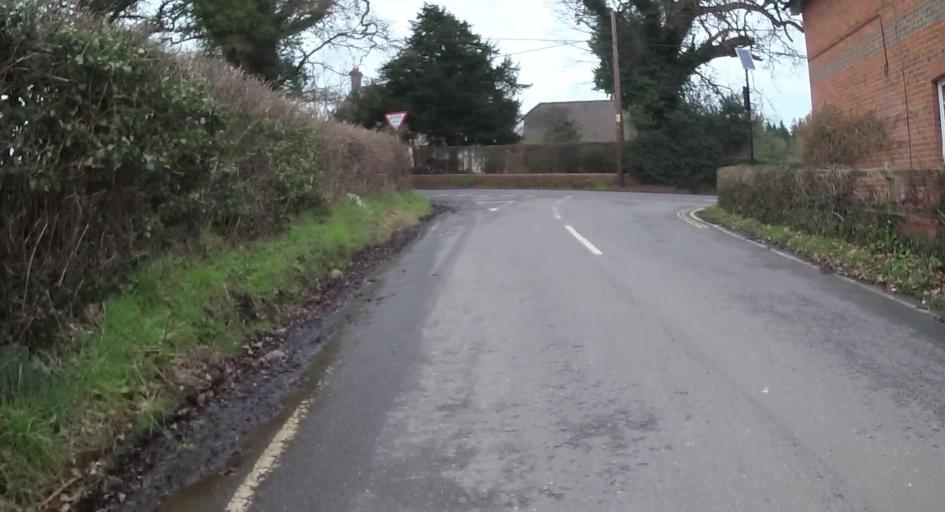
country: GB
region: England
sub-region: West Berkshire
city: Stratfield Mortimer
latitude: 51.3737
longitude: -1.0465
